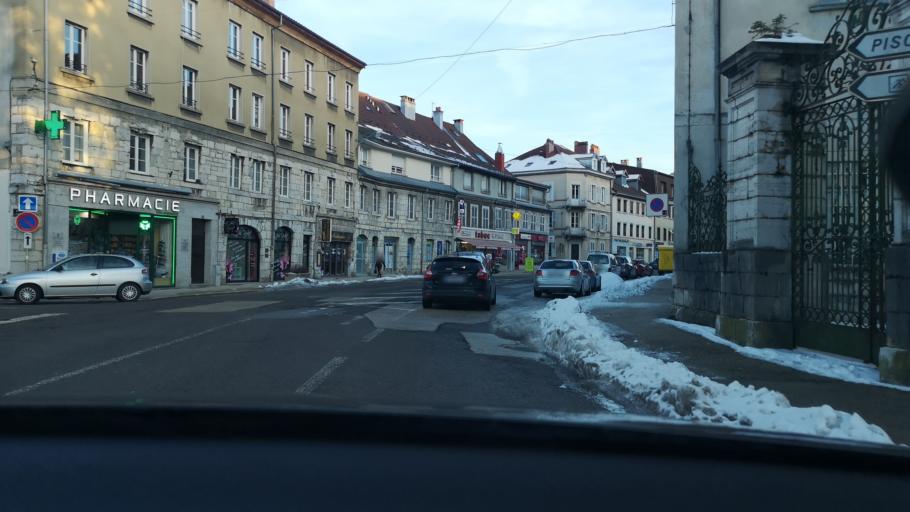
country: FR
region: Franche-Comte
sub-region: Departement du Doubs
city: Pontarlier
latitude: 46.9022
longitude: 6.3590
